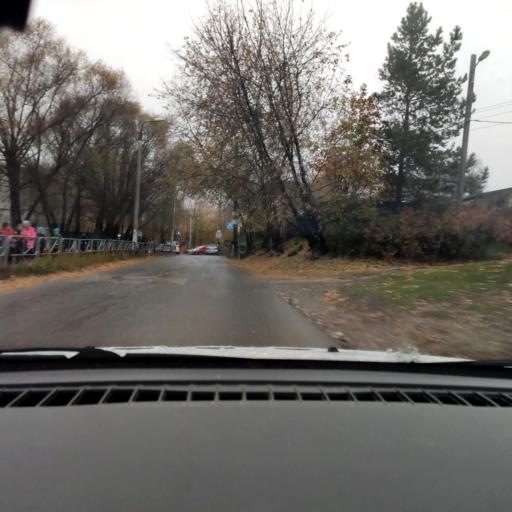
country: RU
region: Perm
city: Kondratovo
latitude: 58.0456
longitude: 56.1051
